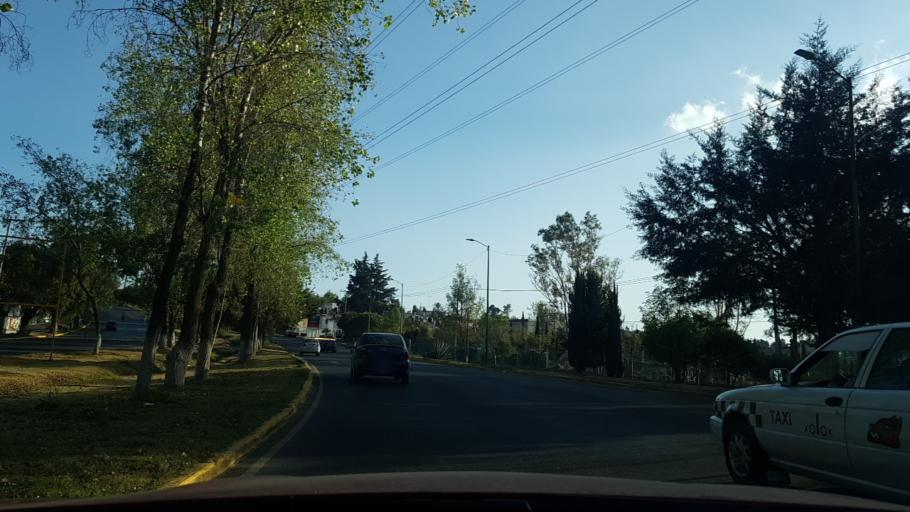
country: MX
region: Mexico
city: Cuautitlan Izcalli
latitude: 19.6460
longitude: -99.2257
